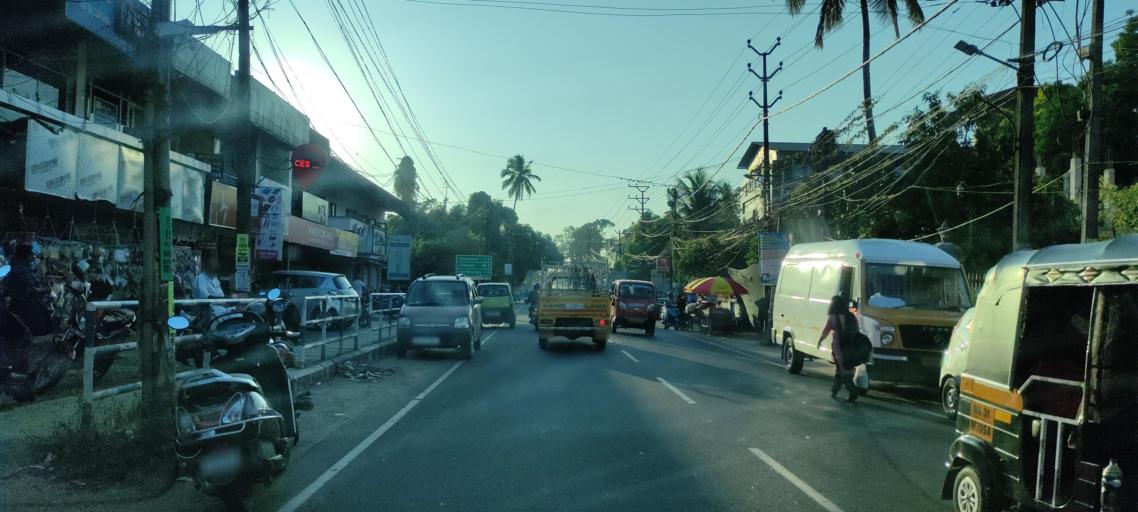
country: IN
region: Kerala
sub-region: Alappuzha
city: Kayankulam
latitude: 9.1753
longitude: 76.5045
